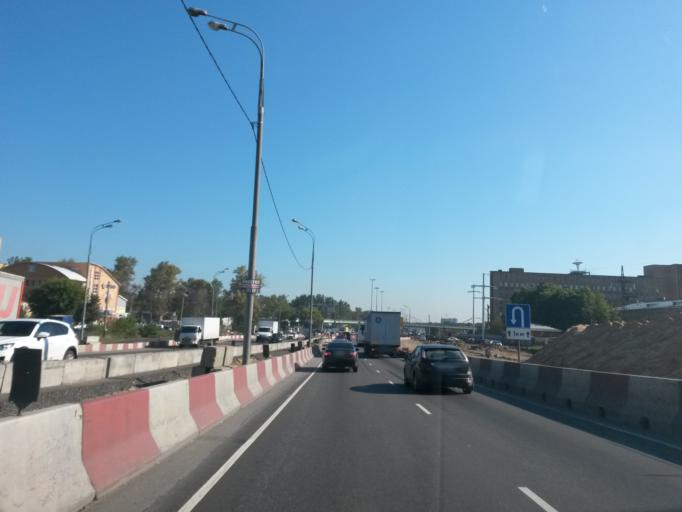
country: RU
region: Moskovskaya
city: Korolev
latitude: 55.9280
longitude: 37.8015
